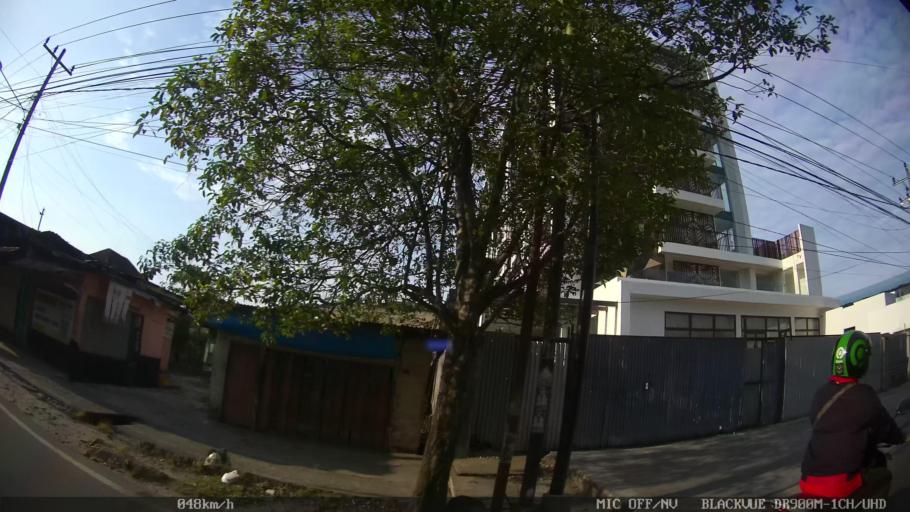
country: ID
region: North Sumatra
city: Medan
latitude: 3.5774
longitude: 98.6457
